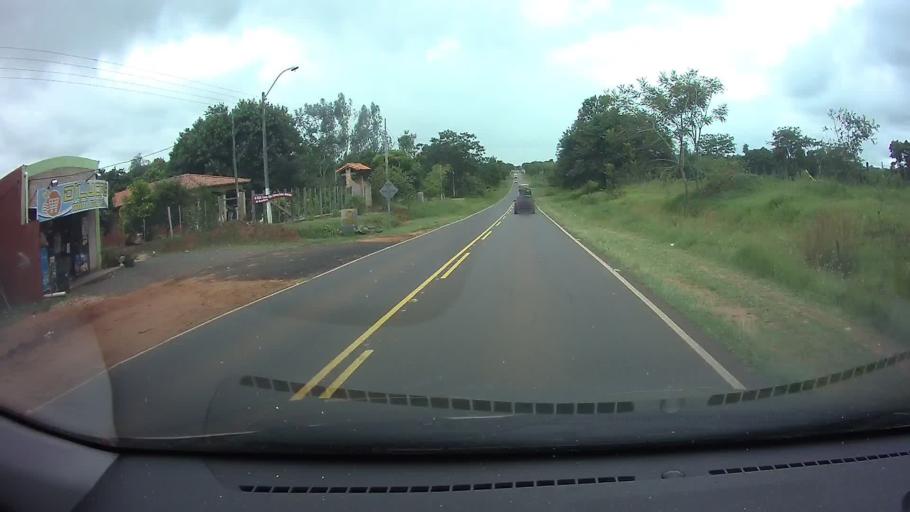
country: PY
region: Paraguari
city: Carapegua
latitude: -25.7466
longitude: -57.2701
